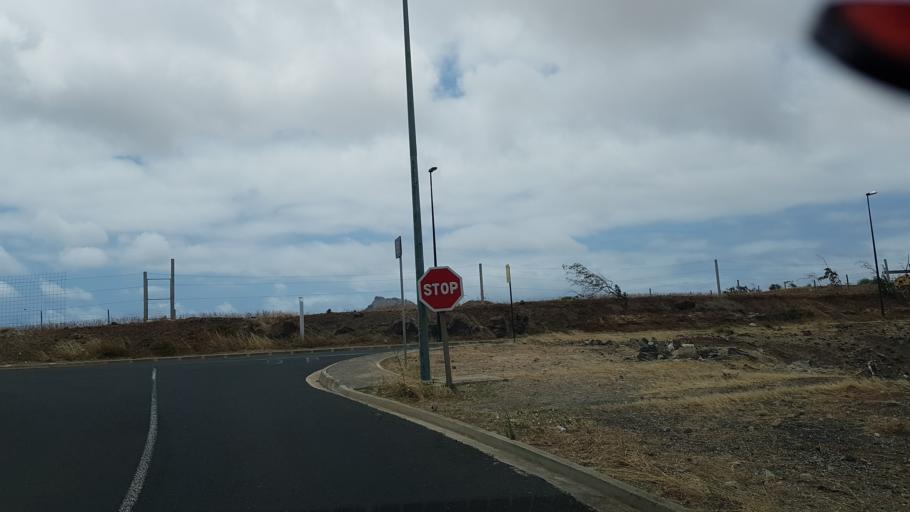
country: PT
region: Madeira
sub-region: Porto Santo
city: Vila de Porto Santo
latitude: 33.0641
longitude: -16.3389
